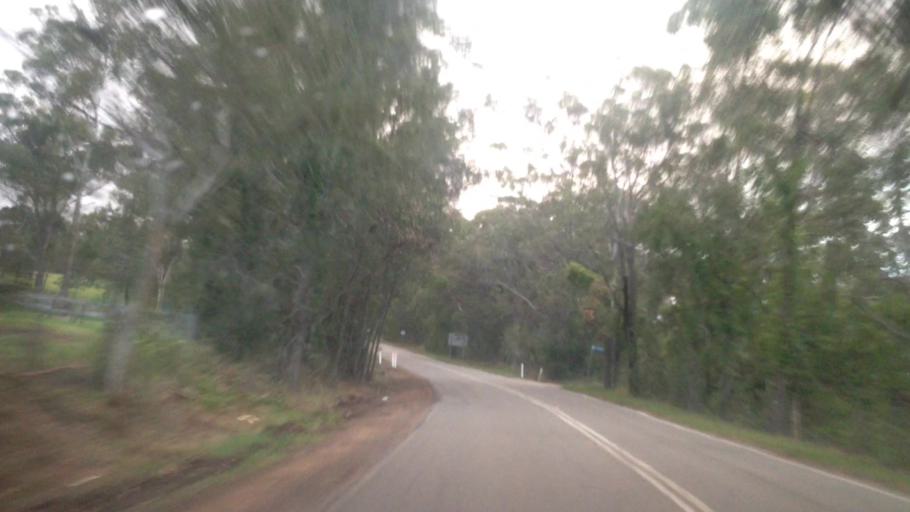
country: AU
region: New South Wales
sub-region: Lake Macquarie Shire
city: Dora Creek
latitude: -33.1081
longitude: 151.4767
